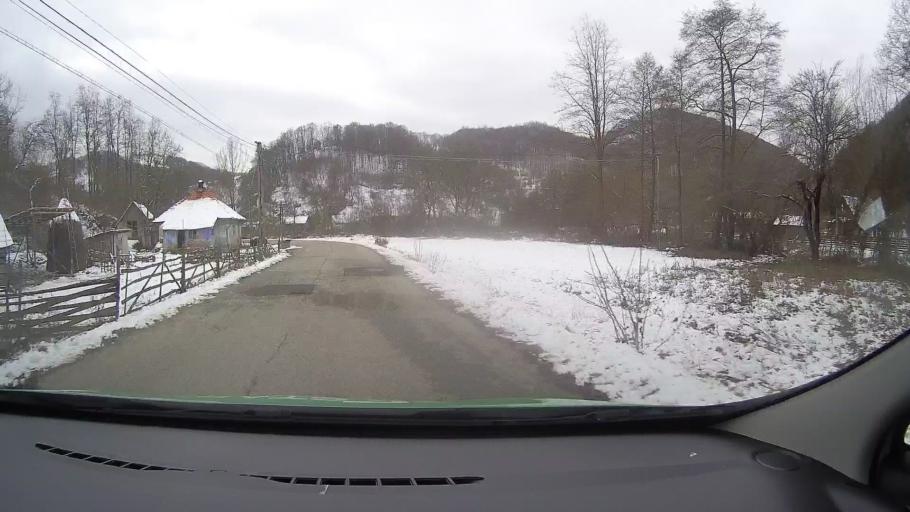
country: RO
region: Hunedoara
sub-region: Comuna Balsa
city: Balsa
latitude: 46.0476
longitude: 23.0693
